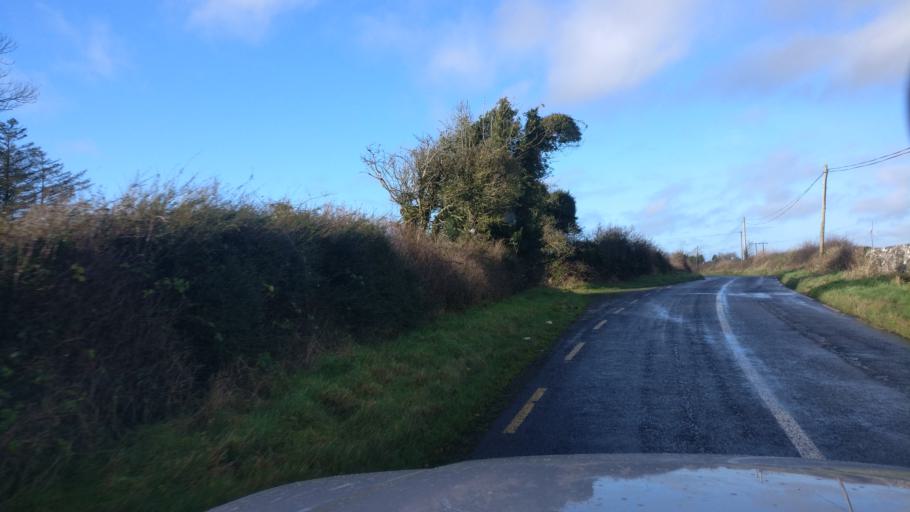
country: IE
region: Connaught
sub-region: County Galway
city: Athenry
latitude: 53.2600
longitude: -8.6810
